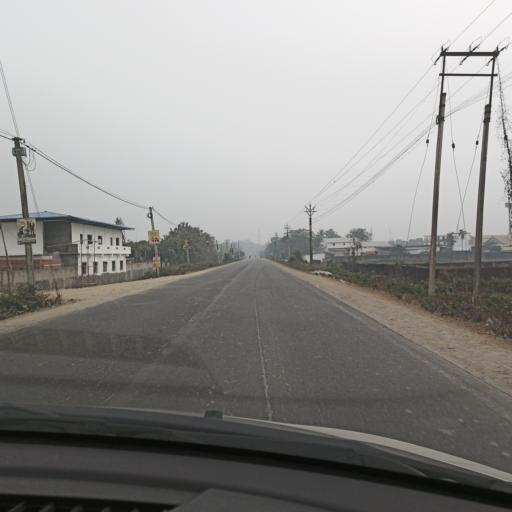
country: IN
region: West Bengal
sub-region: Darjiling
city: Shiliguri
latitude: 26.6759
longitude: 88.4653
